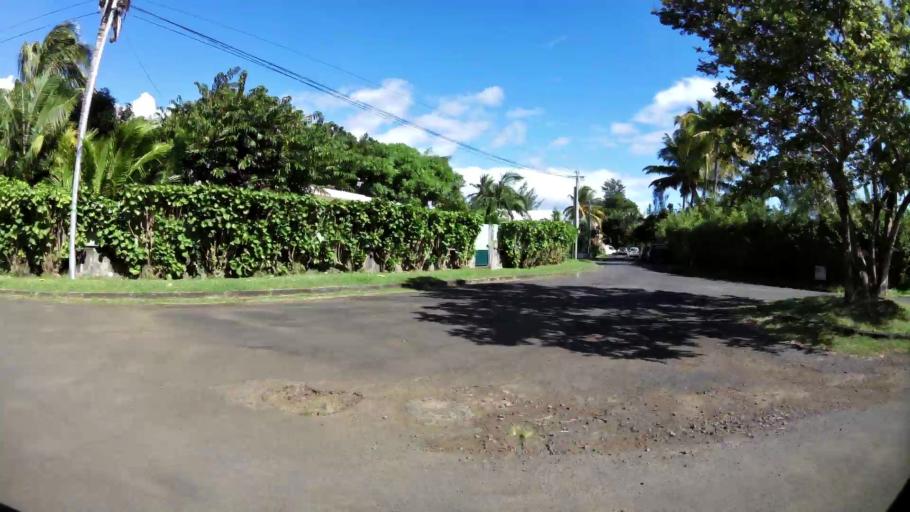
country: RE
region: Reunion
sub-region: Reunion
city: Sainte-Marie
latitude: -20.8993
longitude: 55.5004
